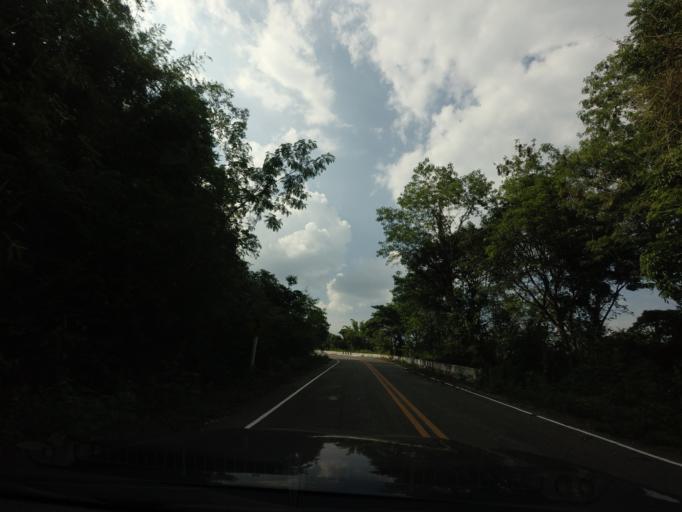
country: TH
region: Nan
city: Na Noi
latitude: 18.2857
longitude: 100.9311
